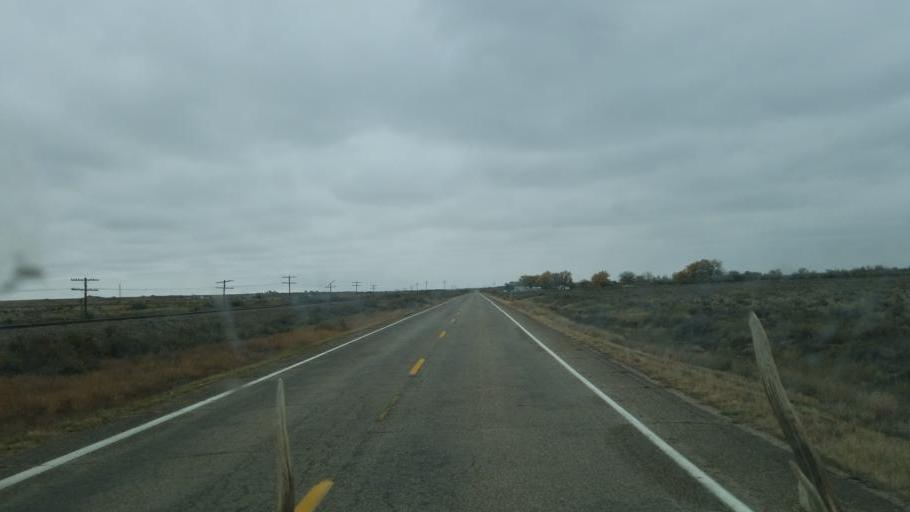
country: US
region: Colorado
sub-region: Otero County
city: Fowler
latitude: 38.2525
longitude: -104.2885
